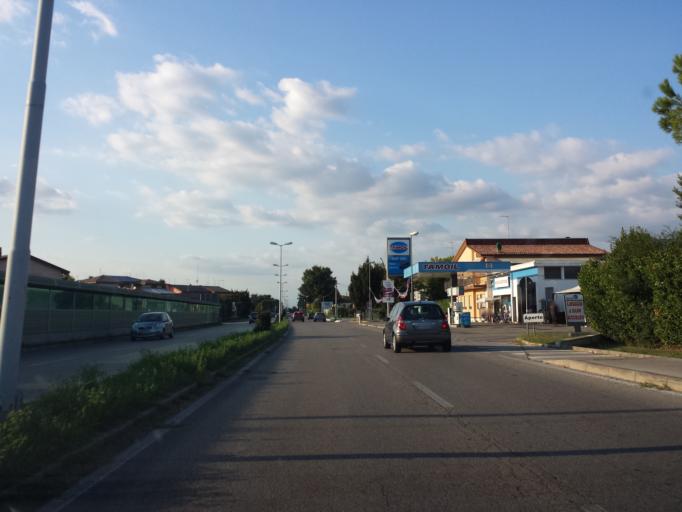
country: IT
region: Veneto
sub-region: Provincia di Padova
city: Padova
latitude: 45.4267
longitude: 11.9002
